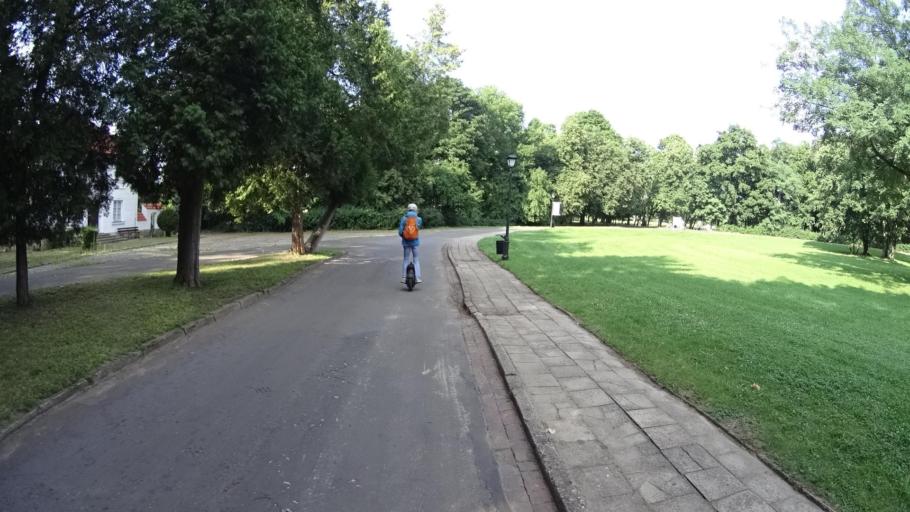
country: PL
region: Masovian Voivodeship
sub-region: Powiat legionowski
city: Jablonna
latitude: 52.3761
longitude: 20.9151
